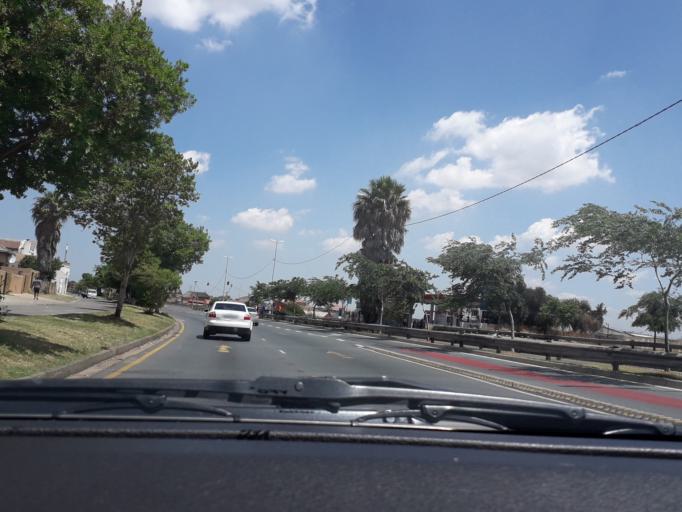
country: ZA
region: Gauteng
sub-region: City of Johannesburg Metropolitan Municipality
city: Johannesburg
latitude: -26.2332
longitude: 27.9511
